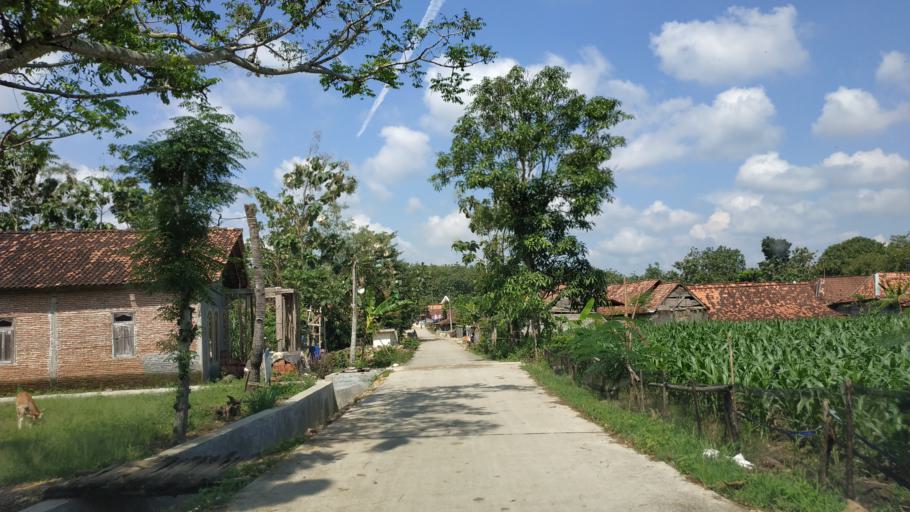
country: ID
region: Central Java
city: Guyangan
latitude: -7.0037
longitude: 111.0911
